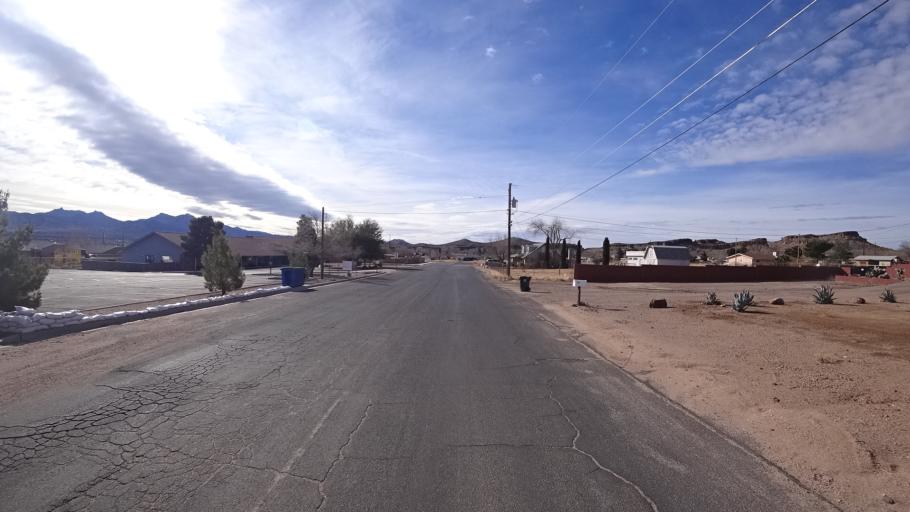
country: US
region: Arizona
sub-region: Mohave County
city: Kingman
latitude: 35.2203
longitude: -114.0493
